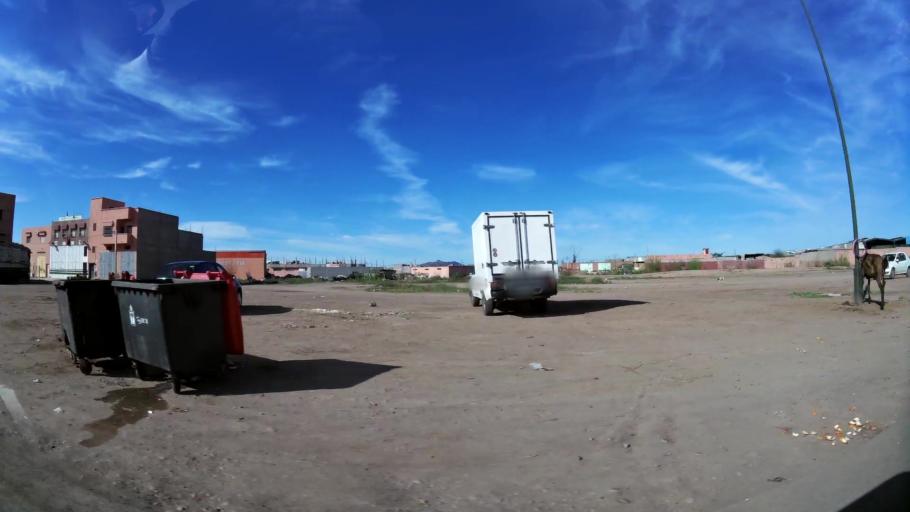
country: MA
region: Marrakech-Tensift-Al Haouz
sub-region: Marrakech
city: Marrakesh
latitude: 31.6823
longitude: -8.0573
